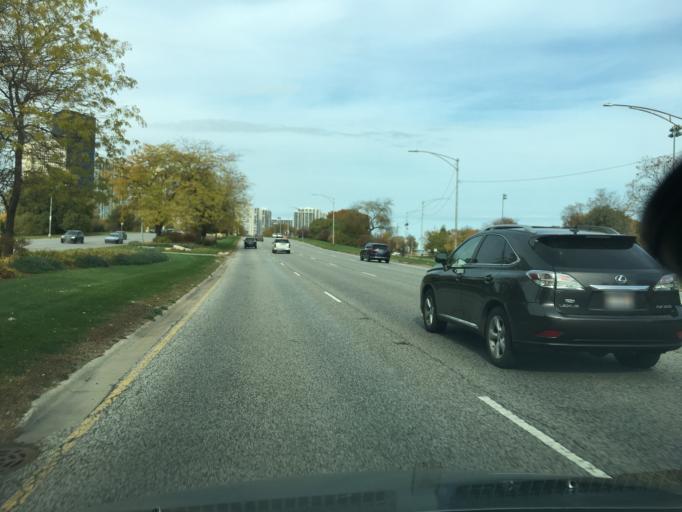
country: US
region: Illinois
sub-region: Cook County
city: Evanston
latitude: 41.9742
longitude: -87.6491
